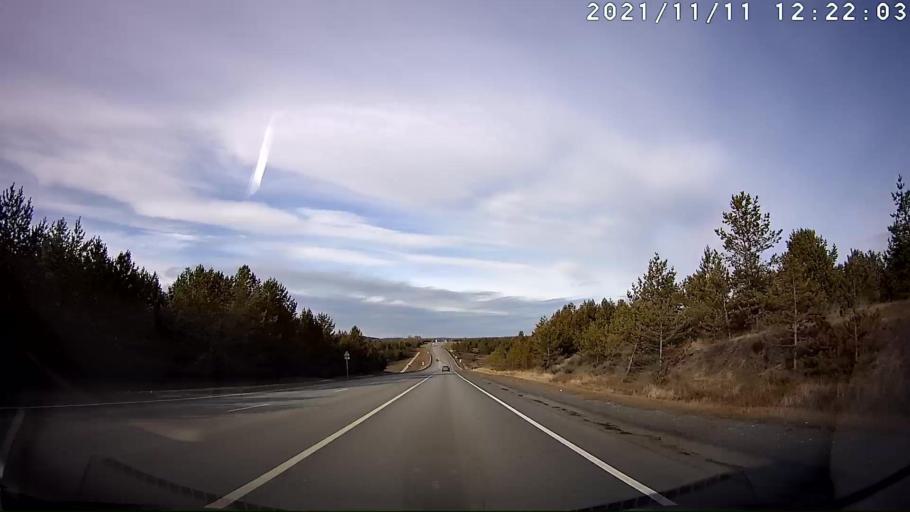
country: RU
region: Ulyanovsk
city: Silikatnyy
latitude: 53.9029
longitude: 48.2564
